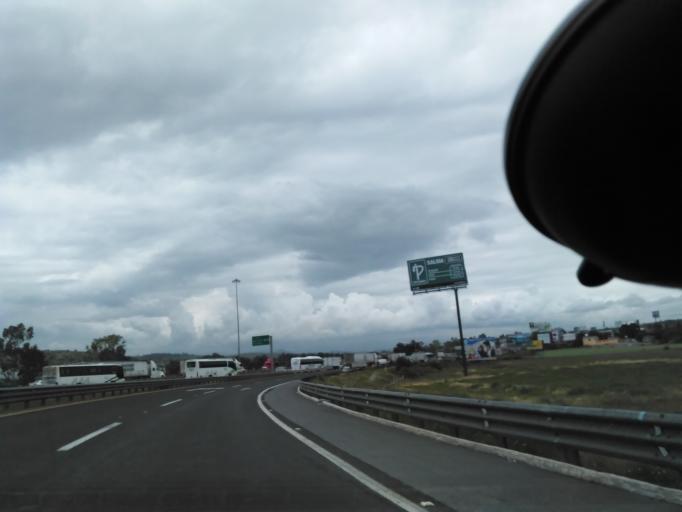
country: MX
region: Mexico
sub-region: Huehuetoca
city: Jorobas
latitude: 19.8194
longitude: -99.2424
